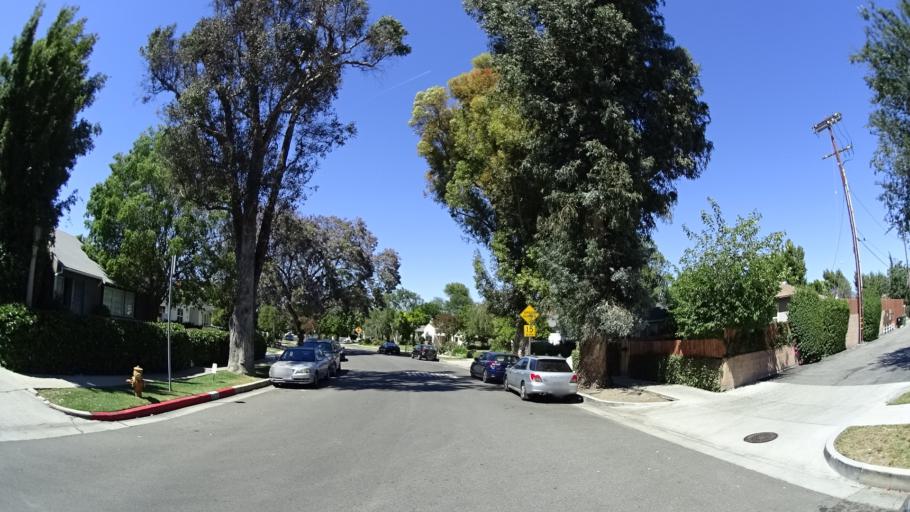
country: US
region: California
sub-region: Los Angeles County
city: Sherman Oaks
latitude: 34.1514
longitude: -118.4445
